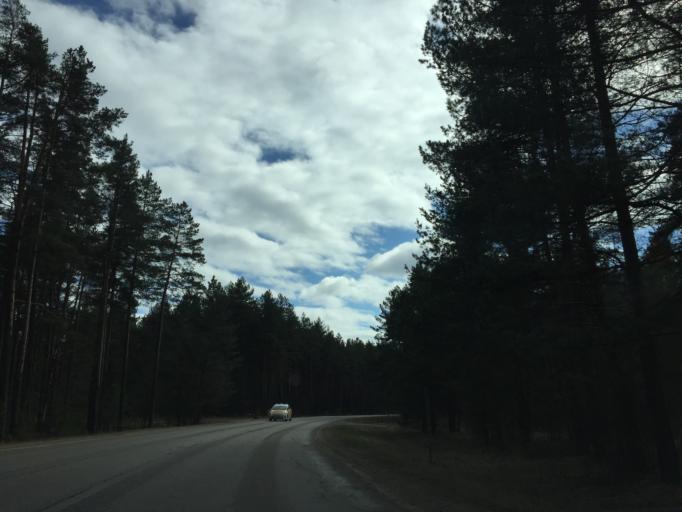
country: LV
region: Stopini
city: Ulbroka
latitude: 56.9537
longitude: 24.3115
